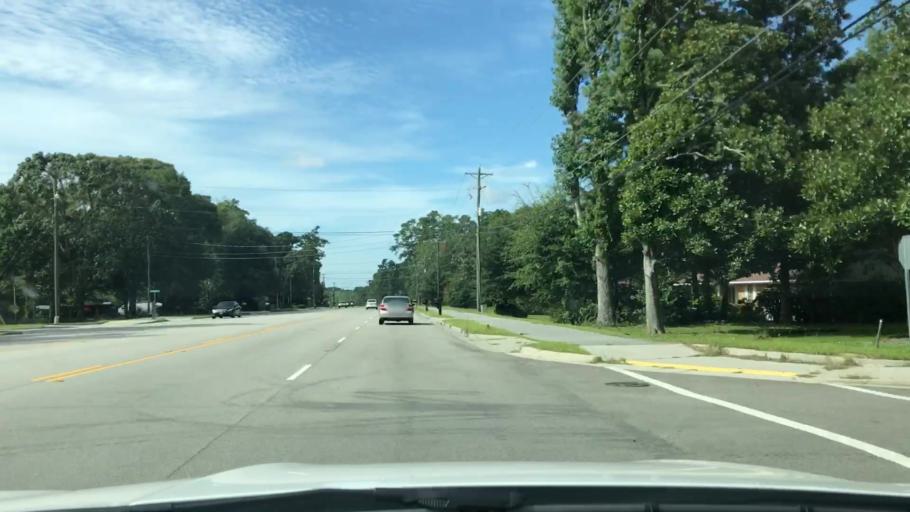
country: US
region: South Carolina
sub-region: Dorchester County
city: Centerville
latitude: 32.9865
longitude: -80.1924
